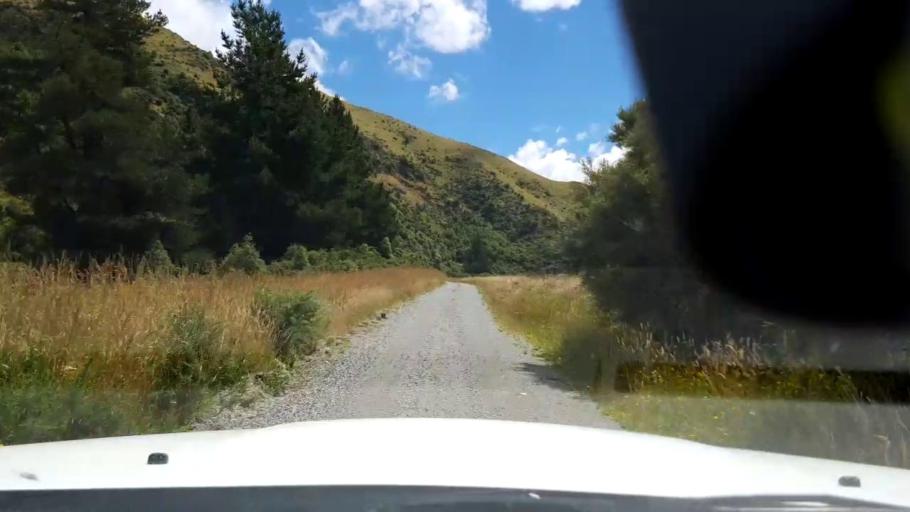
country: NZ
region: Canterbury
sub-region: Timaru District
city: Pleasant Point
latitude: -43.9324
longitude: 171.1951
